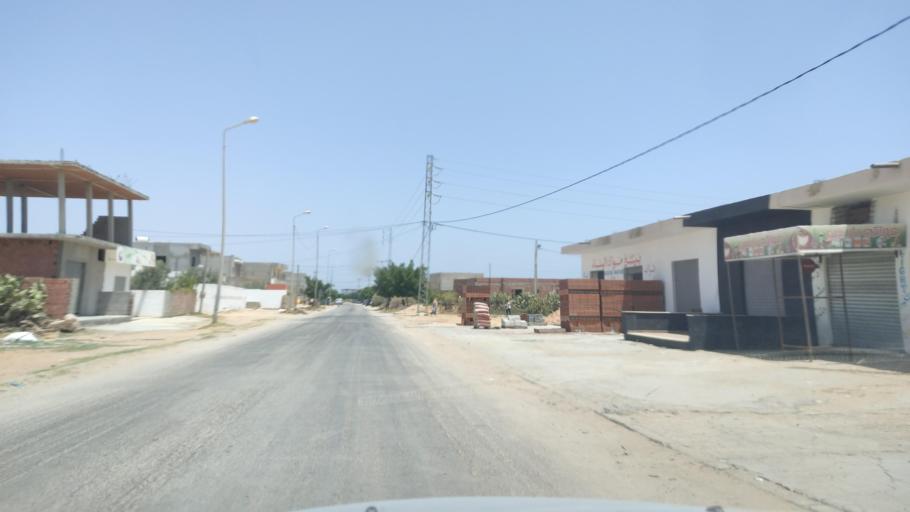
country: TN
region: Safaqis
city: Sfax
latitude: 34.6651
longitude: 10.7080
